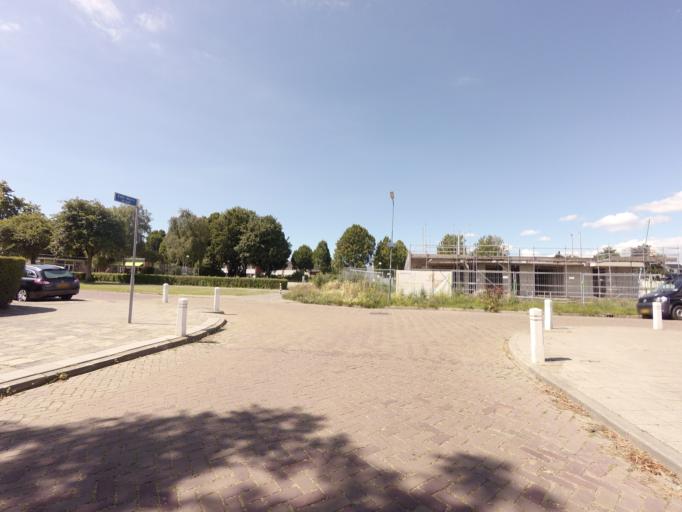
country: NL
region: Utrecht
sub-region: Gemeente Woerden
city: Woerden
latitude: 52.0889
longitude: 4.8670
